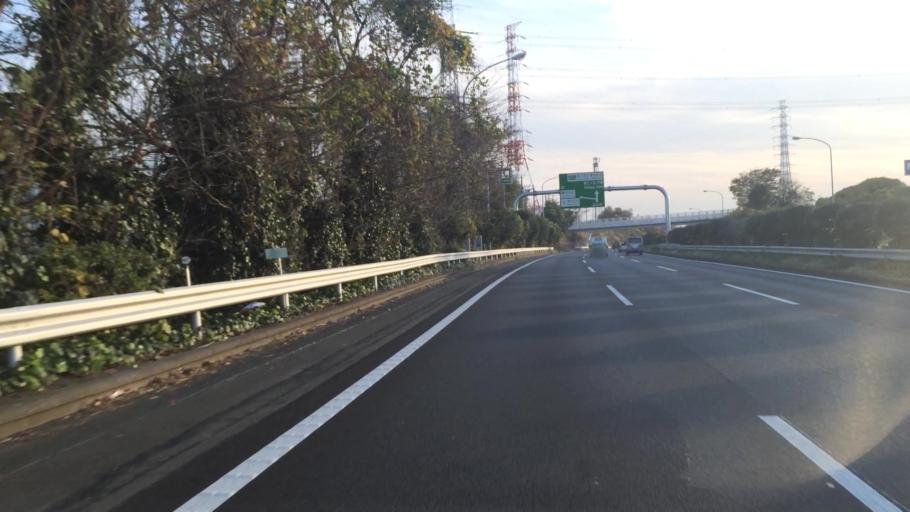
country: JP
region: Kanagawa
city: Yokohama
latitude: 35.5374
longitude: 139.6017
